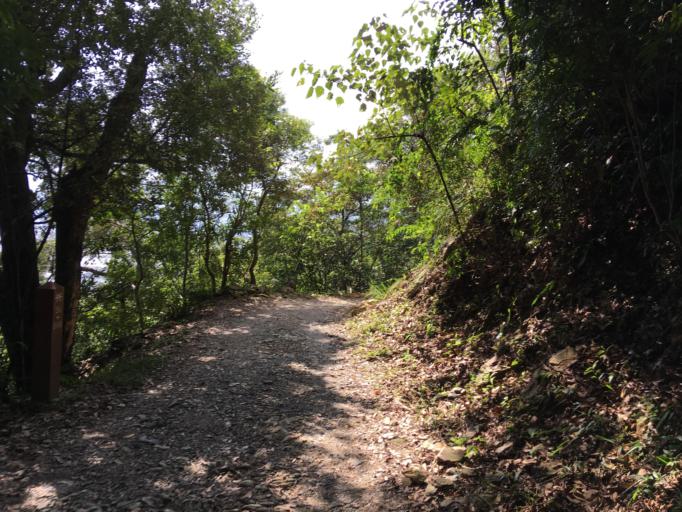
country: TW
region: Taiwan
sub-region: Yilan
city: Yilan
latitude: 24.8434
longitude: 121.7773
